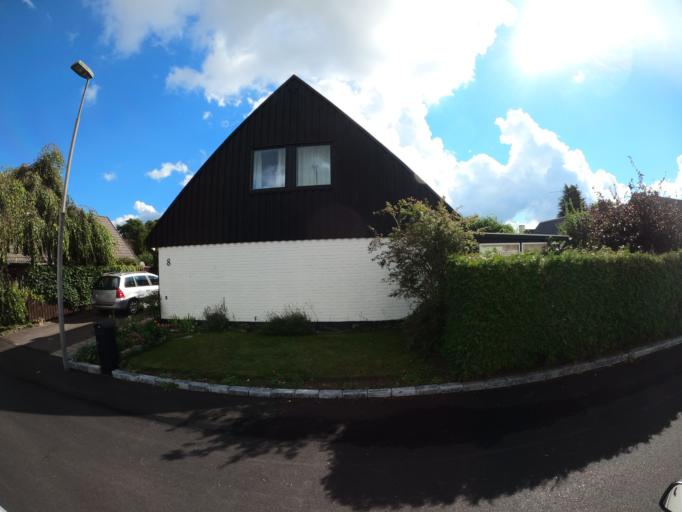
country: SE
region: Skane
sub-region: Lunds Kommun
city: Genarp
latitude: 55.6027
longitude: 13.3934
